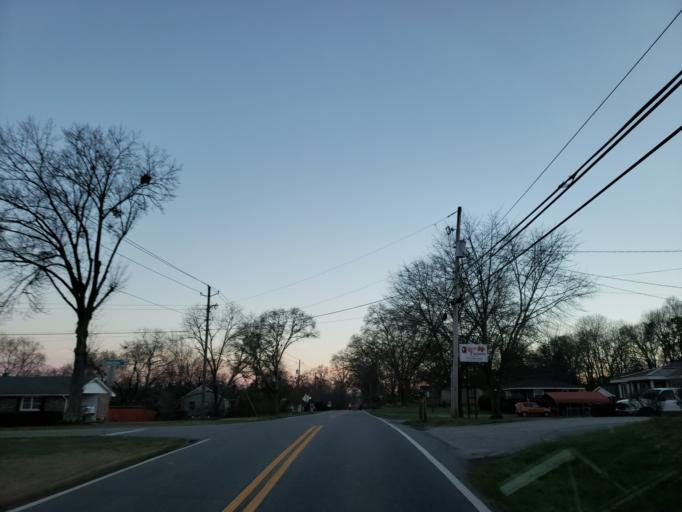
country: US
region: Georgia
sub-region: Bartow County
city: Cartersville
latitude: 34.1961
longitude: -84.8196
